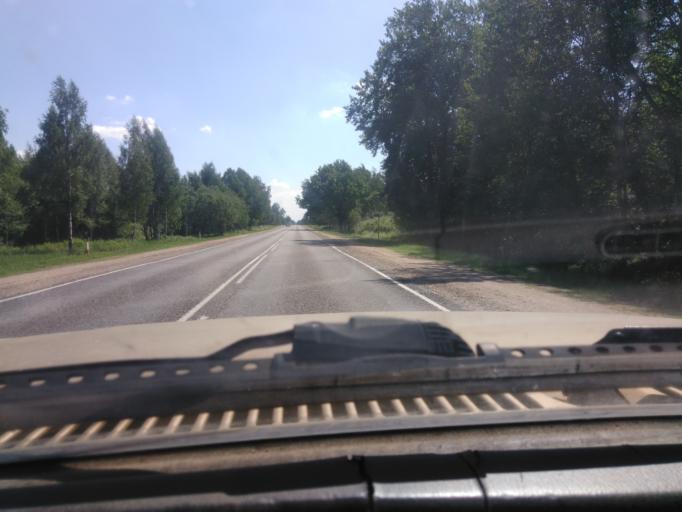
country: BY
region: Mogilev
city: Palykavichy Pyershyya
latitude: 54.0078
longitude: 30.3206
